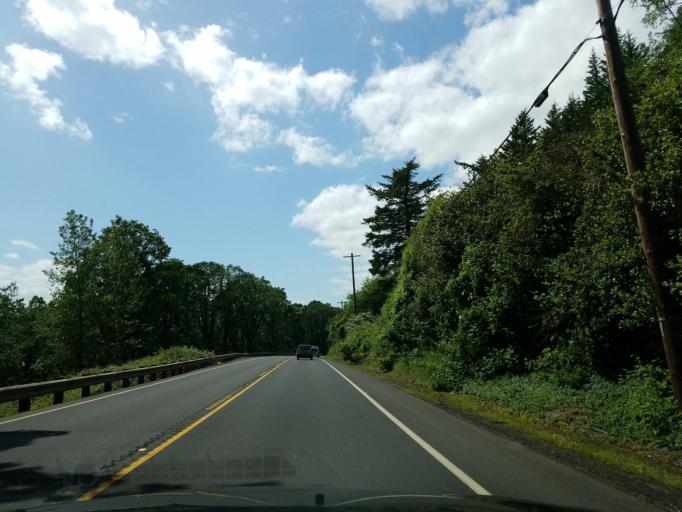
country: US
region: Washington
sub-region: Clark County
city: Washougal
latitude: 45.5598
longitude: -122.2576
